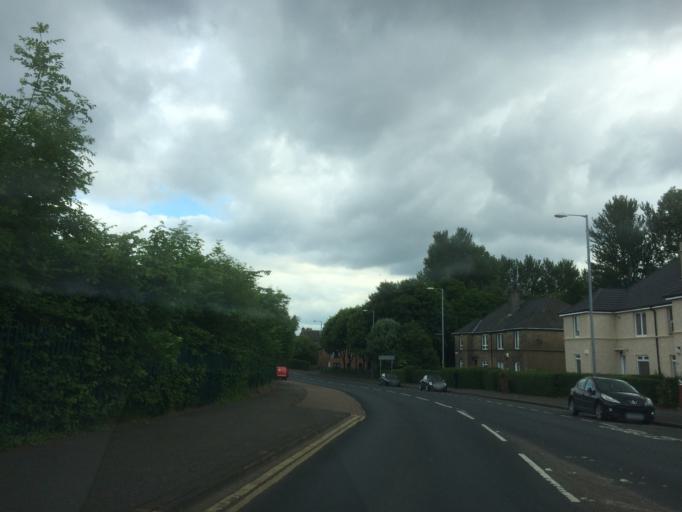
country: GB
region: Scotland
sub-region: Glasgow City
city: Glasgow
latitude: 55.8301
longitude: -4.2562
